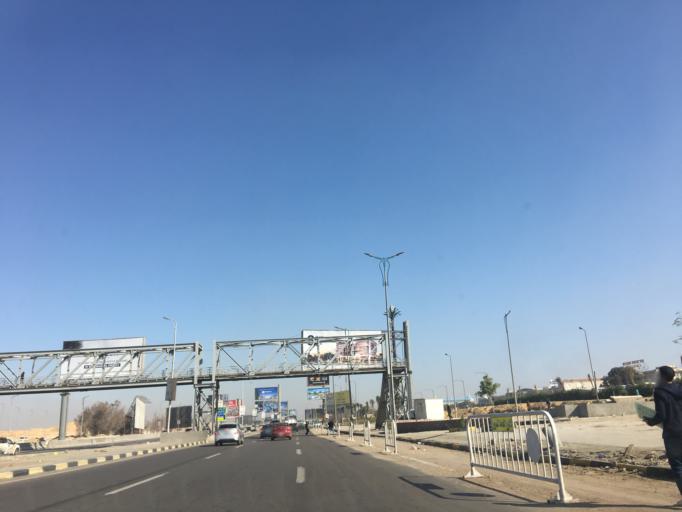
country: EG
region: Muhafazat al Qalyubiyah
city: Al Khankah
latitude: 30.0549
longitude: 31.4123
